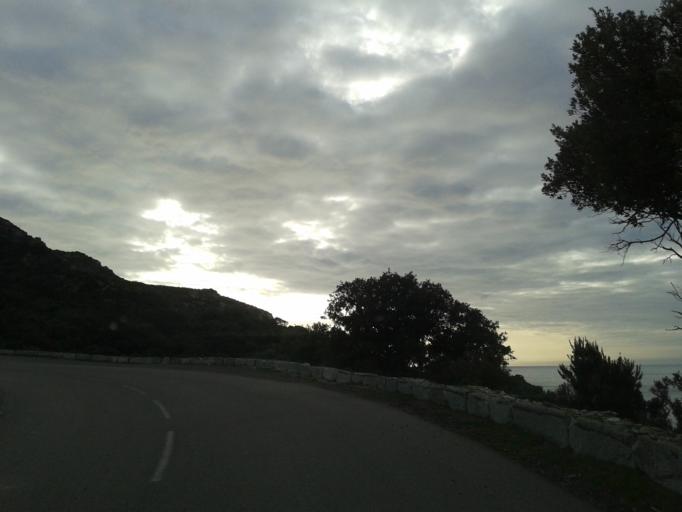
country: FR
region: Corsica
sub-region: Departement de la Haute-Corse
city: Brando
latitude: 42.8647
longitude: 9.3437
